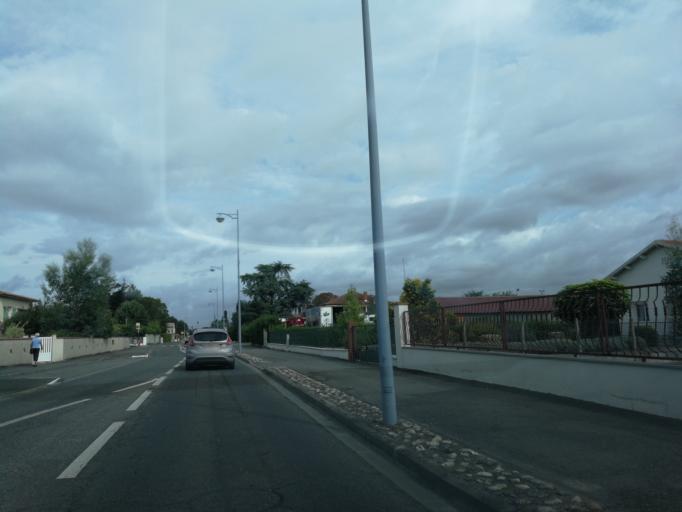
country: FR
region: Midi-Pyrenees
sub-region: Departement de la Haute-Garonne
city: Saint-Alban
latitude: 43.6862
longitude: 1.4180
